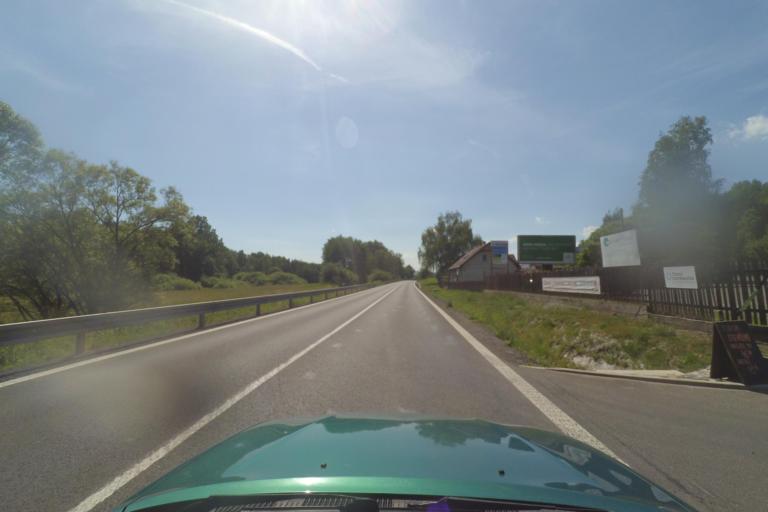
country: CZ
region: Liberecky
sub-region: Okres Ceska Lipa
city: Ceska Lipa
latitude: 50.6815
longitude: 14.5750
